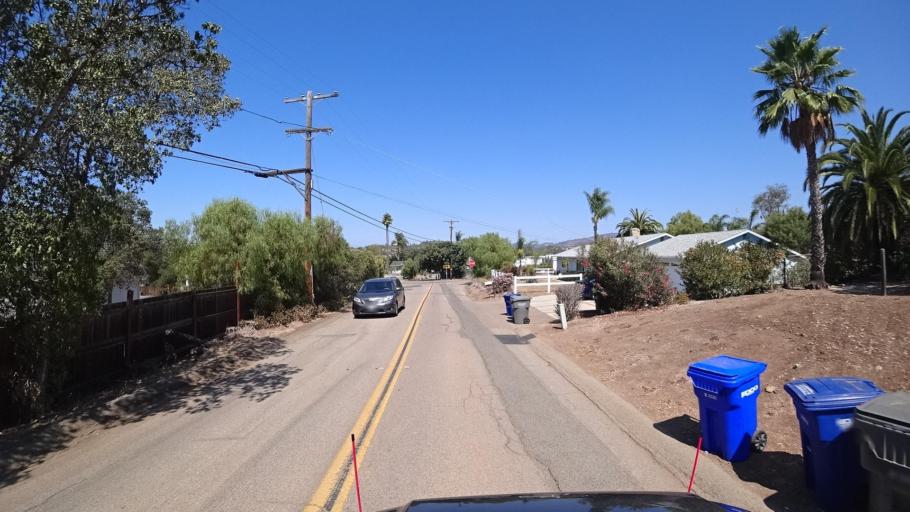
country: US
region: California
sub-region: San Diego County
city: Lake San Marcos
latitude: 33.1698
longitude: -117.2018
